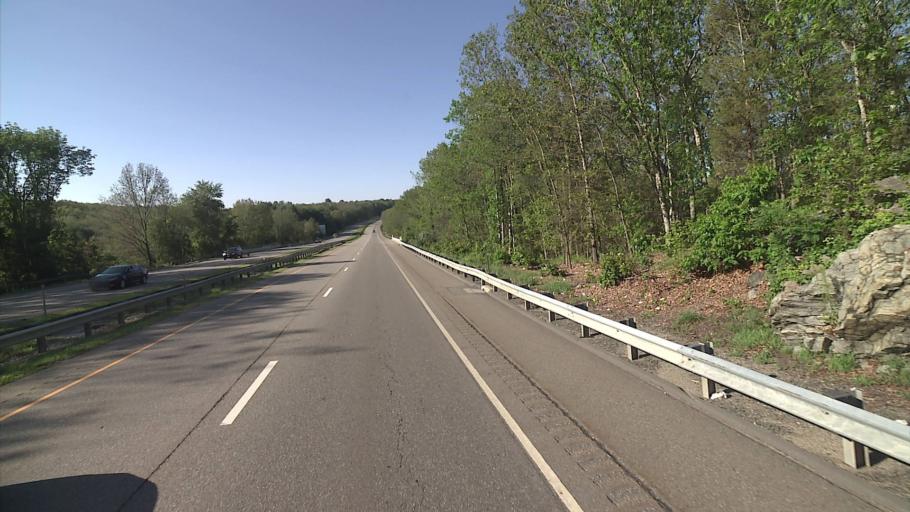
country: US
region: Connecticut
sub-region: Windham County
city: Wauregan
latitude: 41.7455
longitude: -71.8796
